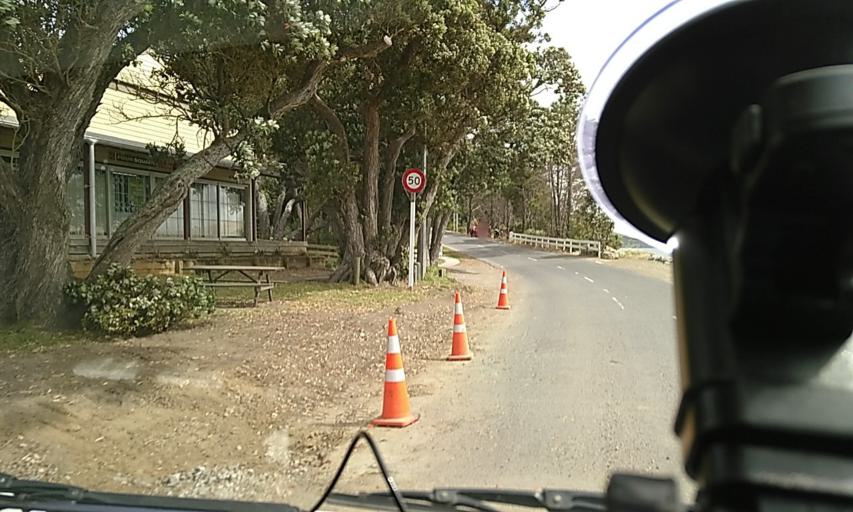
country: NZ
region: Northland
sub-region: Far North District
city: Ahipara
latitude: -35.5055
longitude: 173.3905
